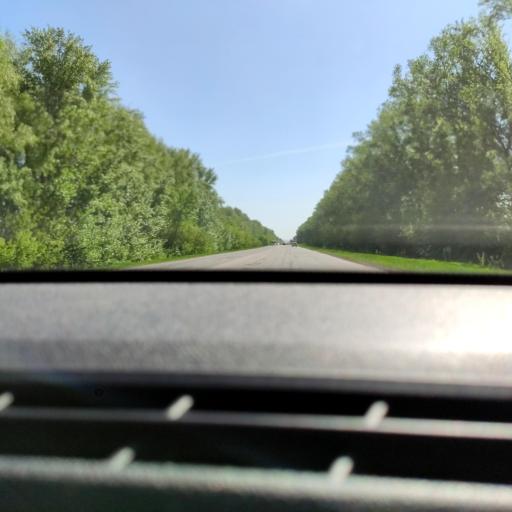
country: RU
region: Samara
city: Tol'yatti
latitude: 53.6296
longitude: 49.4170
